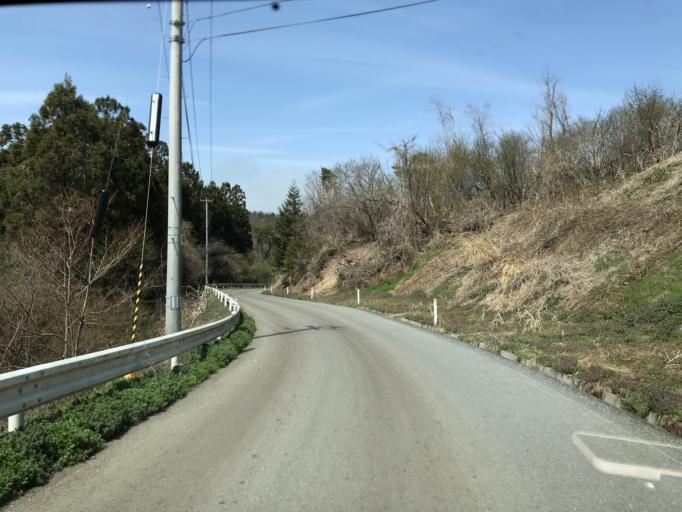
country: JP
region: Iwate
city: Ichinoseki
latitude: 38.8025
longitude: 141.2693
